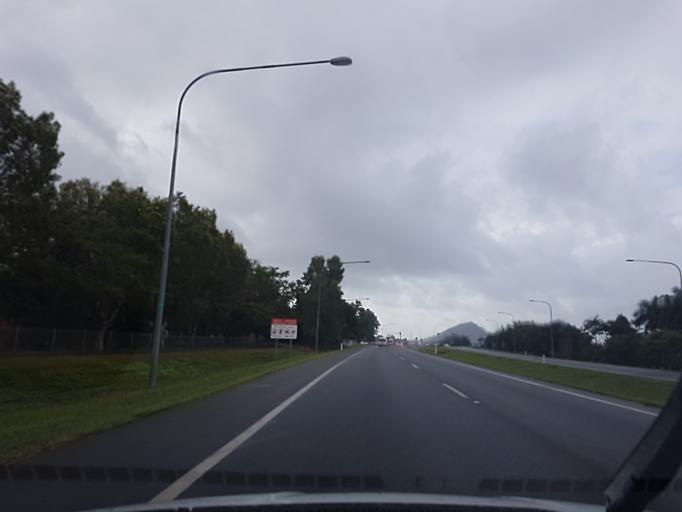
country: AU
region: Queensland
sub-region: Cairns
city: Yorkeys Knob
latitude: -16.8342
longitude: 145.6932
